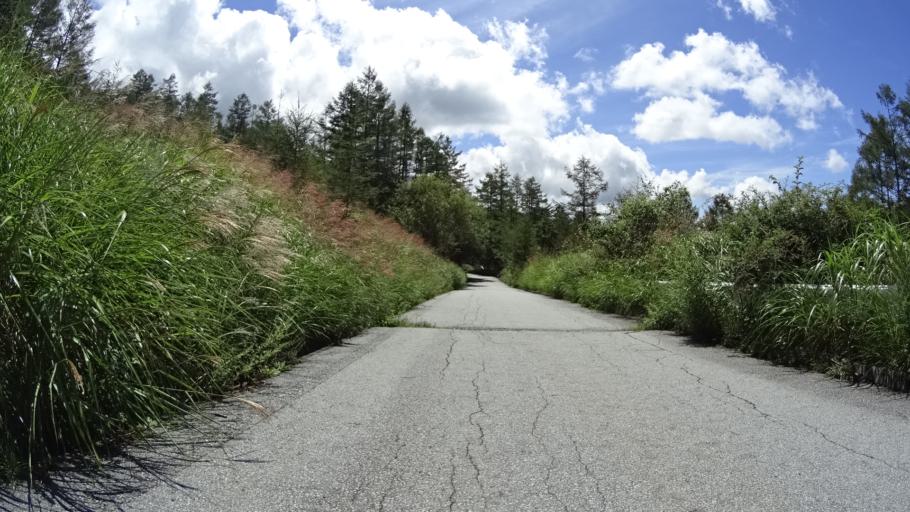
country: JP
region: Yamanashi
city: Enzan
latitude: 35.7272
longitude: 138.8428
